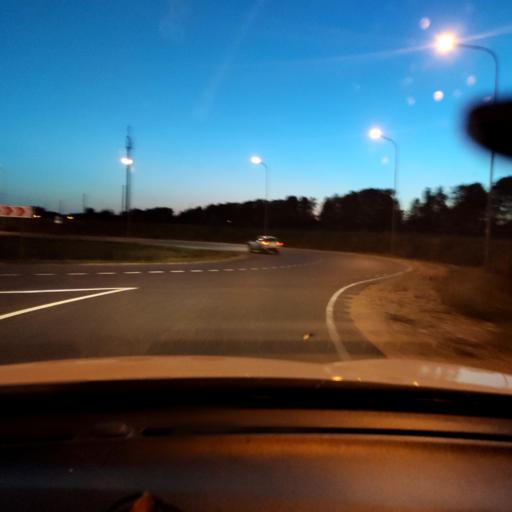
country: RU
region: Tatarstan
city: Osinovo
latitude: 55.8579
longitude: 48.8405
